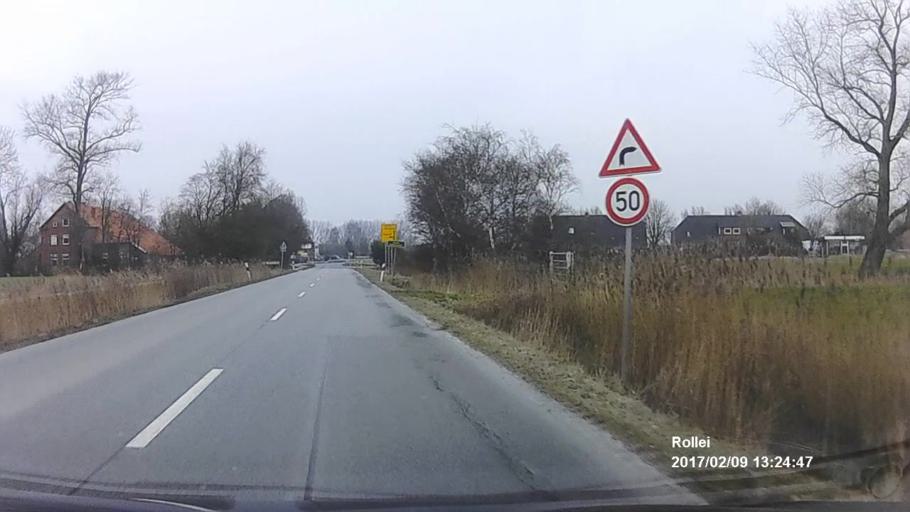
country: DE
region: Lower Saxony
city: Wirdum
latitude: 53.4693
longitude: 7.1385
